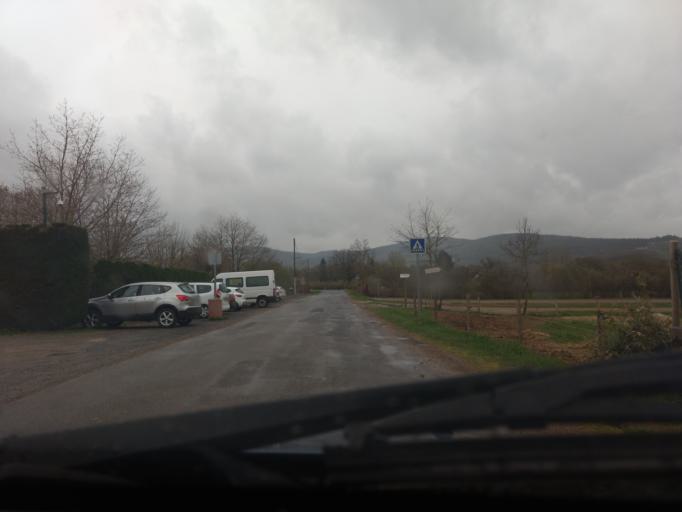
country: FR
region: Midi-Pyrenees
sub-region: Departement de l'Aveyron
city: La Loubiere
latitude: 44.3934
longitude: 2.6910
